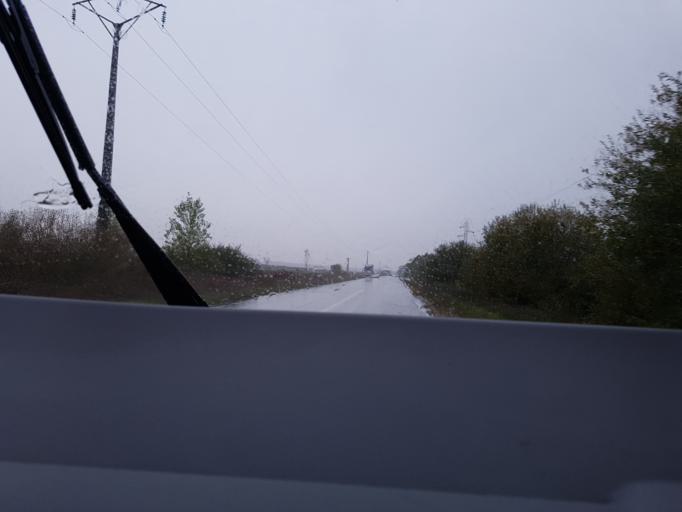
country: FR
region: Aquitaine
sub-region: Departement de la Gironde
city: Saint-Louis-de-Montferrand
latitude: 44.9560
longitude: -0.5180
